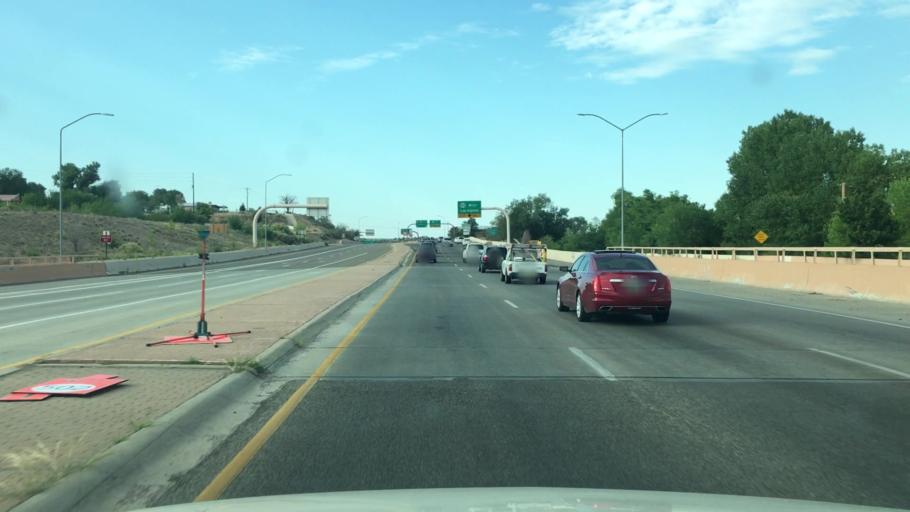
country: US
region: New Mexico
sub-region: Santa Fe County
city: Pojoaque
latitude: 35.8970
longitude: -106.0214
